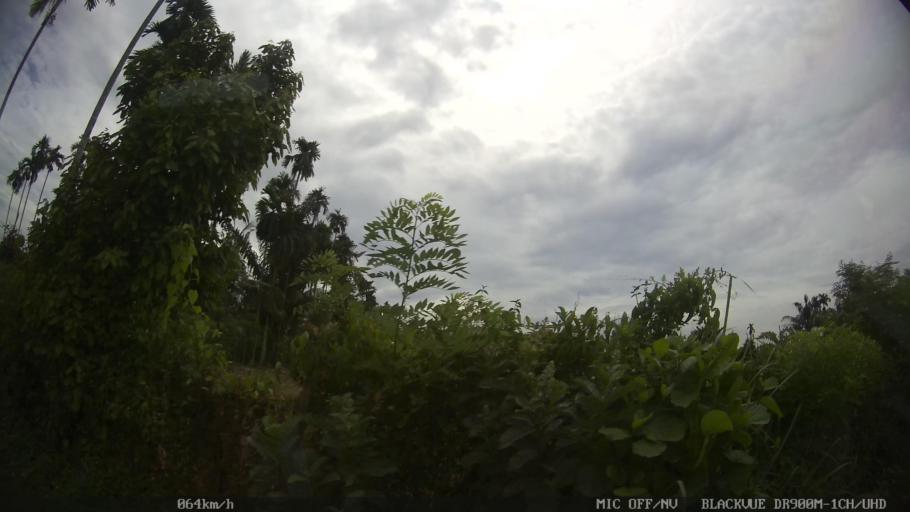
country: ID
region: North Sumatra
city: Sunggal
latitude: 3.5744
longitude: 98.5773
